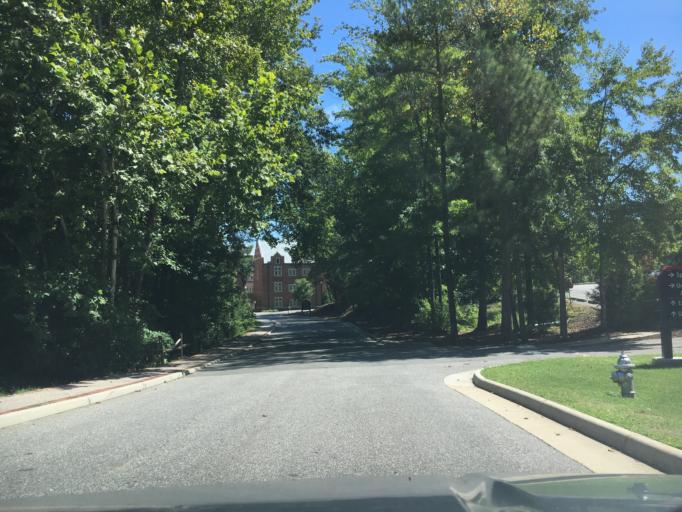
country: US
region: Virginia
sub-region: Henrico County
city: Tuckahoe
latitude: 37.5722
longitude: -77.5412
